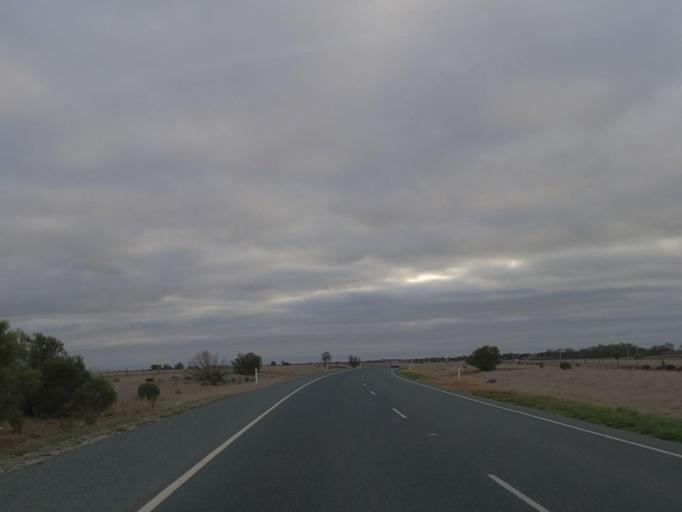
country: AU
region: Victoria
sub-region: Swan Hill
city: Swan Hill
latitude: -35.6263
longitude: 143.8087
